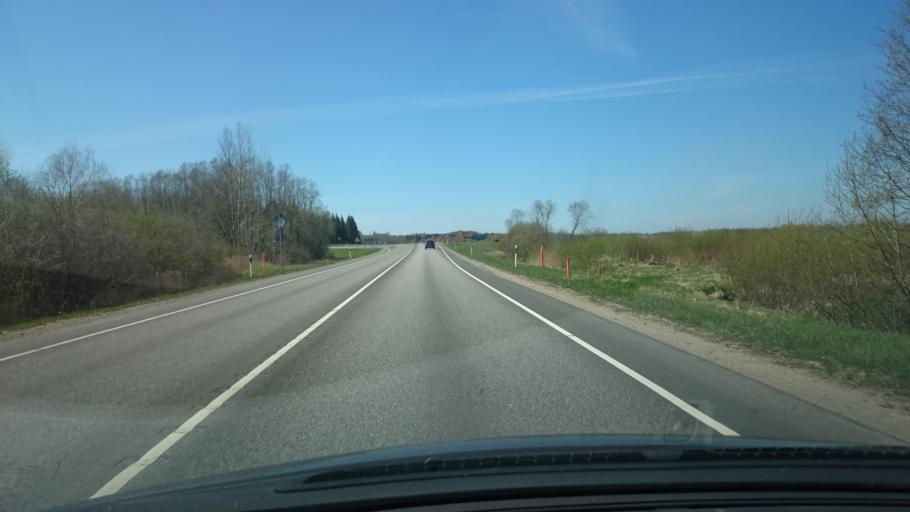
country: EE
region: Ida-Virumaa
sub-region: Narva-Joesuu linn
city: Narva-Joesuu
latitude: 59.3761
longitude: 27.9353
